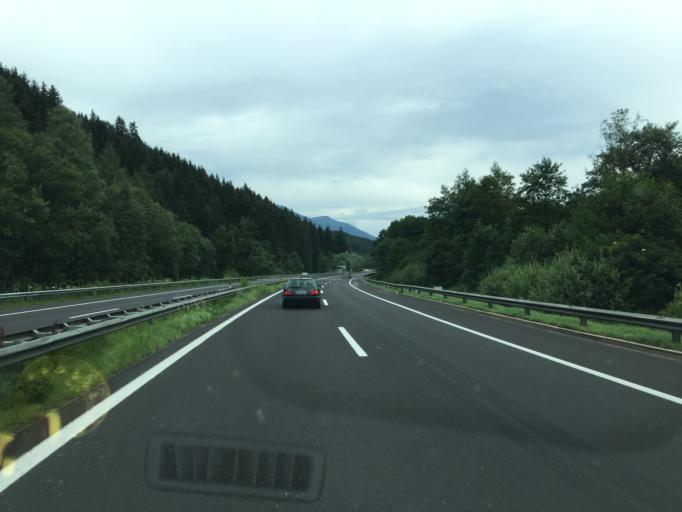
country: AT
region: Styria
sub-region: Politischer Bezirk Liezen
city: Treglwang
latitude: 47.4796
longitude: 14.5531
